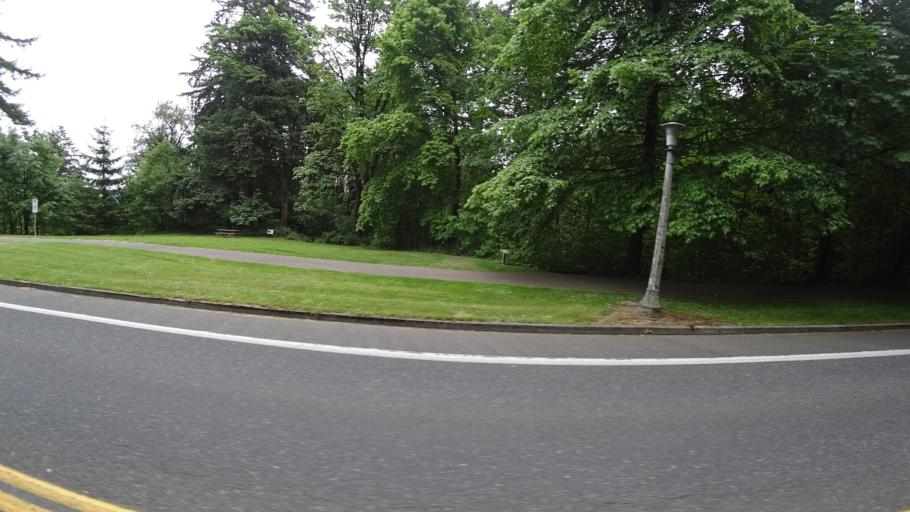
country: US
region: Oregon
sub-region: Multnomah County
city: Portland
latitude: 45.4874
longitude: -122.6853
